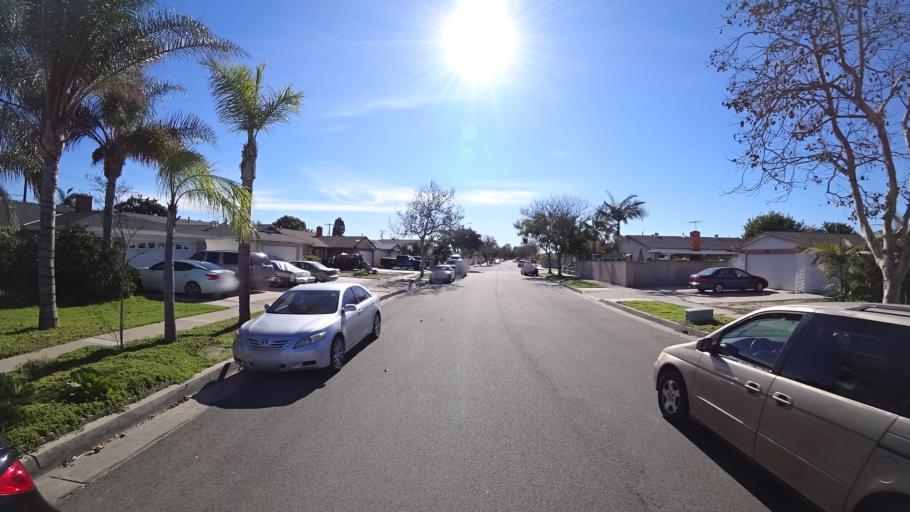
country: US
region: California
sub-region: Orange County
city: Garden Grove
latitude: 33.7552
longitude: -117.9360
